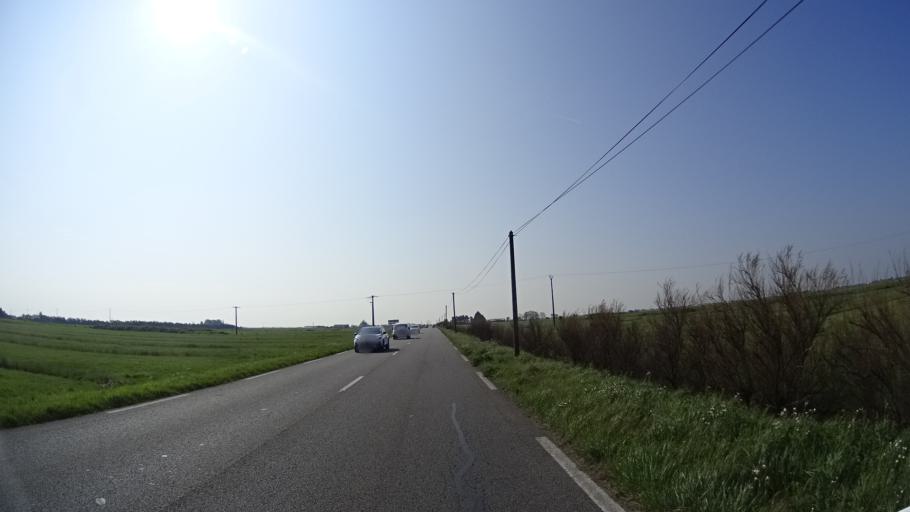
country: FR
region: Pays de la Loire
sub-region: Departement de la Loire-Atlantique
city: Bourgneuf-en-Retz
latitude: 47.0189
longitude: -1.9593
